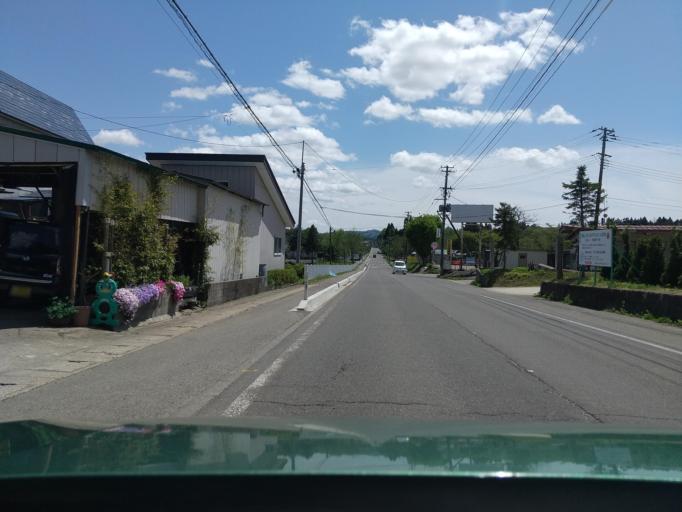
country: JP
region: Akita
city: Yokotemachi
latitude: 39.3448
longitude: 140.5631
